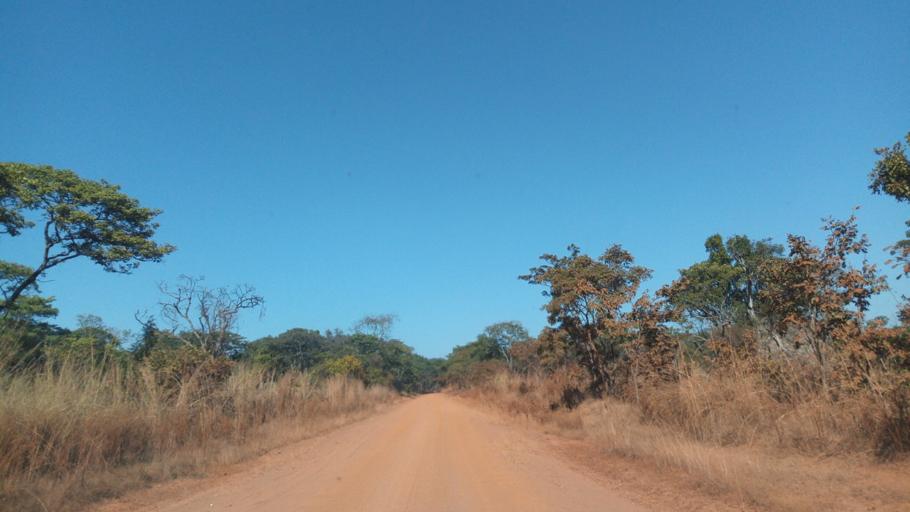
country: ZM
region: Luapula
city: Mwense
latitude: -10.6927
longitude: 28.3883
